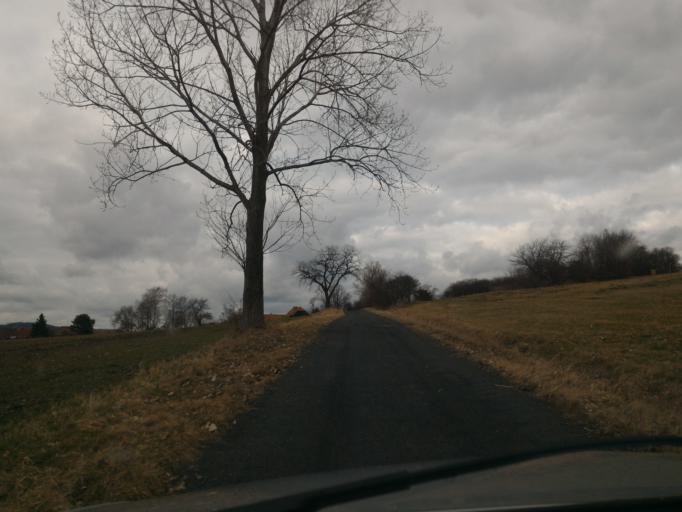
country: CZ
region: Ustecky
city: Varnsdorf
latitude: 50.8930
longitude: 14.6375
